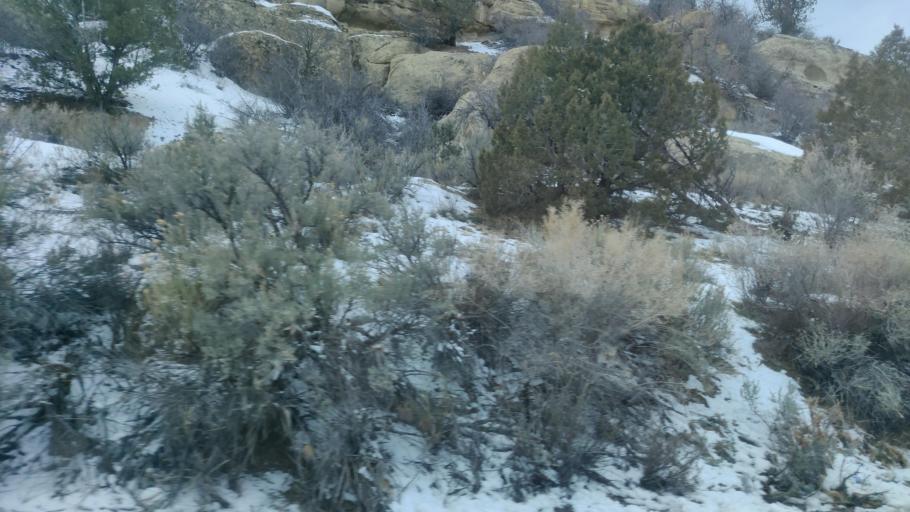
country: US
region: Colorado
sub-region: Mesa County
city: Palisade
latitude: 39.1956
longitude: -108.1402
